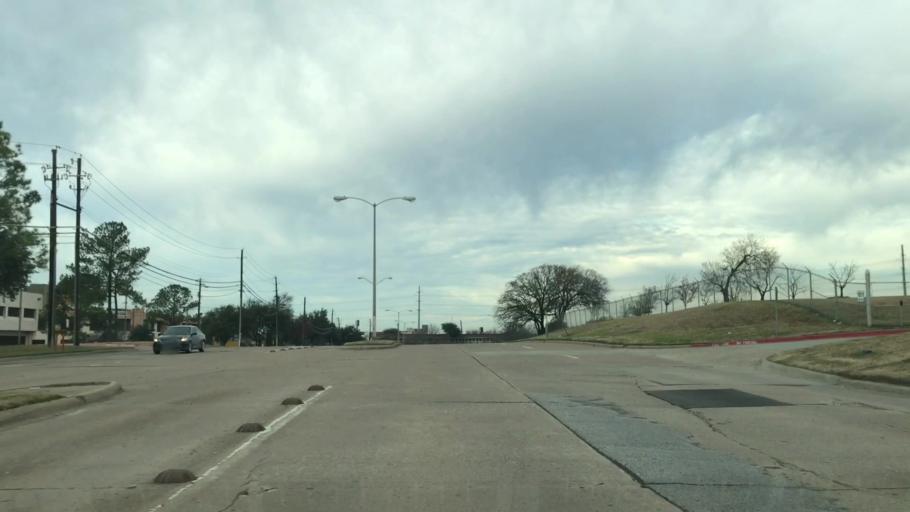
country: US
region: Texas
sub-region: Dallas County
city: University Park
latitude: 32.8370
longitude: -96.8700
